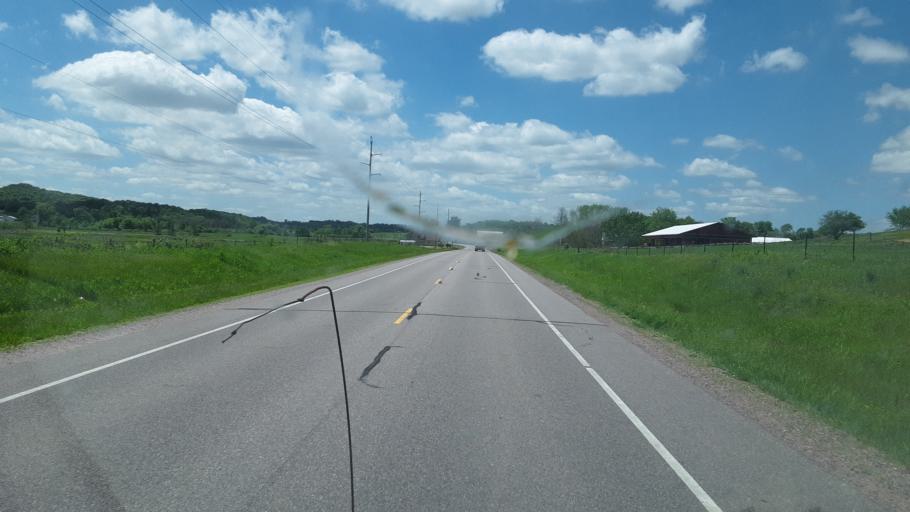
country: US
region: Wisconsin
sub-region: Sauk County
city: Reedsburg
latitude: 43.5932
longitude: -89.9205
